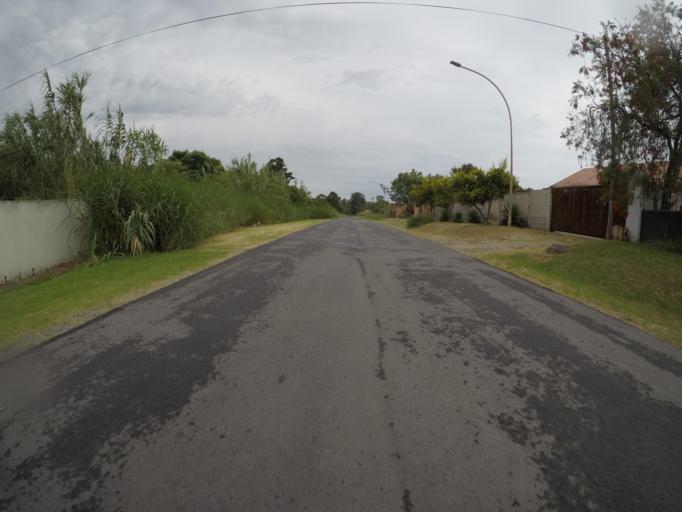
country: ZA
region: Eastern Cape
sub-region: Buffalo City Metropolitan Municipality
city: East London
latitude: -32.9657
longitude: 27.8334
